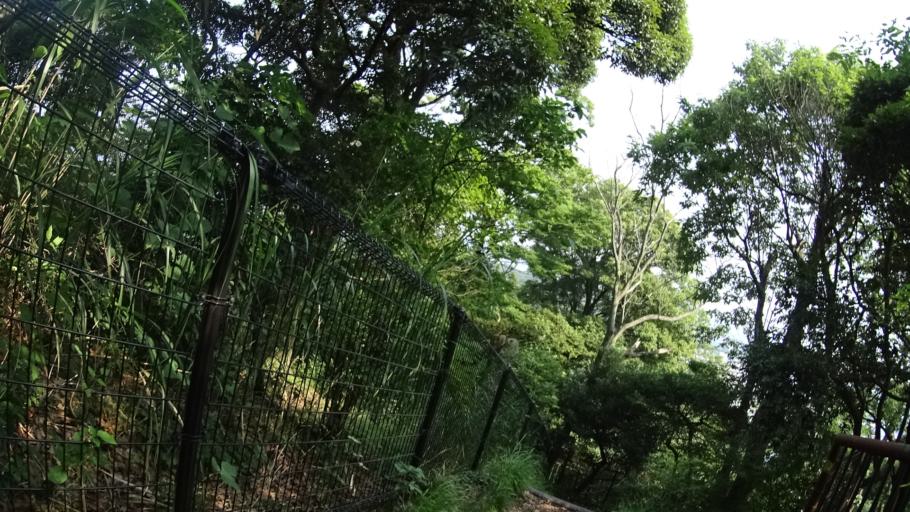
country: JP
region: Kanagawa
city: Zushi
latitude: 35.3067
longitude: 139.6126
